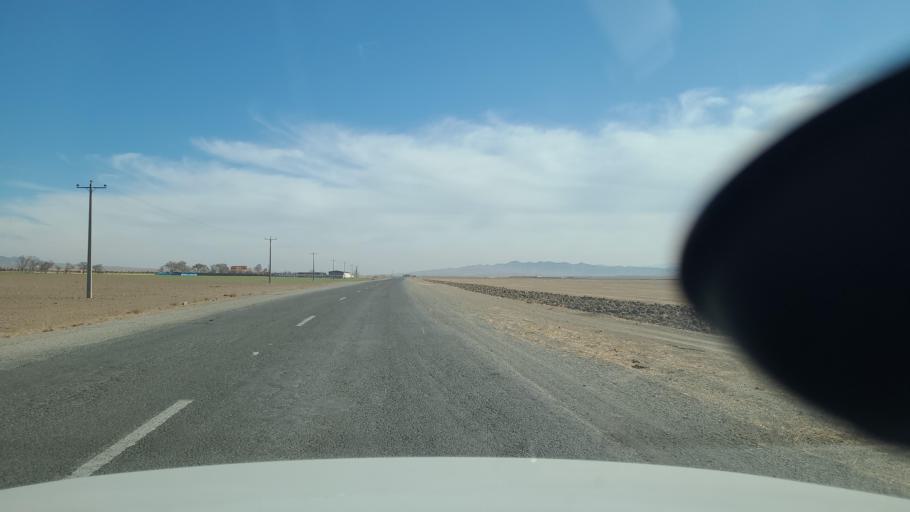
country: IR
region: Razavi Khorasan
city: Dowlatabad
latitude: 35.5998
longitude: 59.4653
